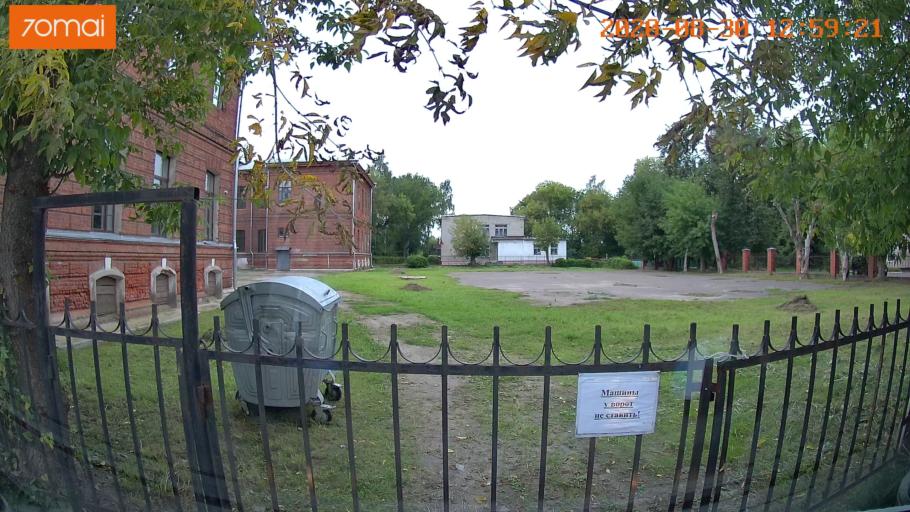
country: RU
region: Ivanovo
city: Kineshma
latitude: 57.4458
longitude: 42.1555
